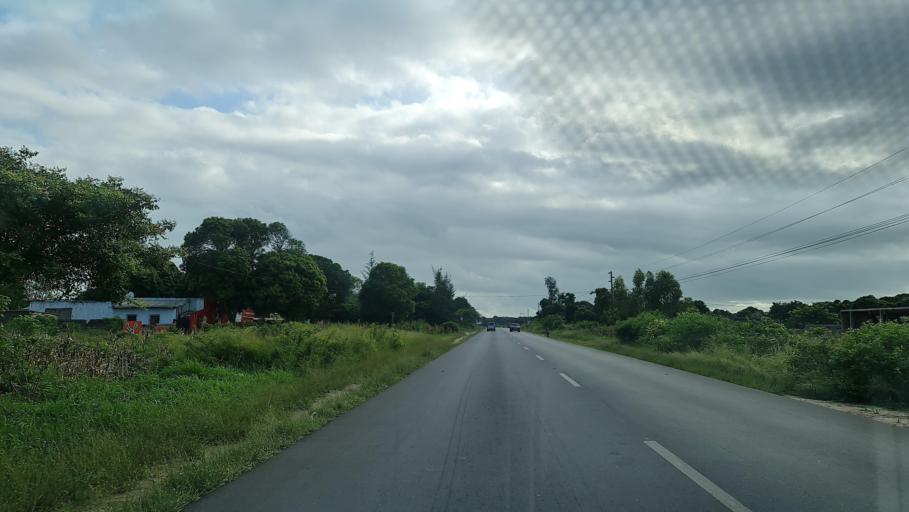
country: MZ
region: Maputo
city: Manhica
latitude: -25.4140
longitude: 32.7390
